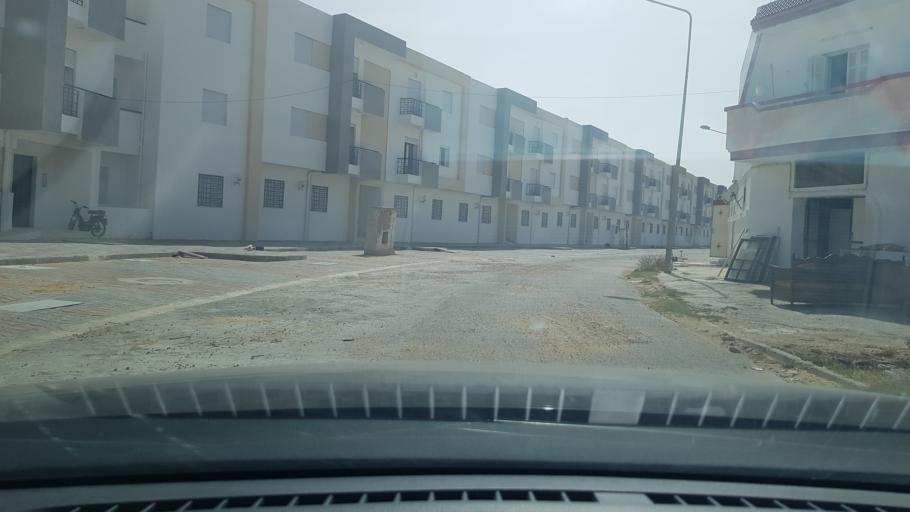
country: TN
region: Safaqis
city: Al Qarmadah
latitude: 34.8314
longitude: 10.7534
